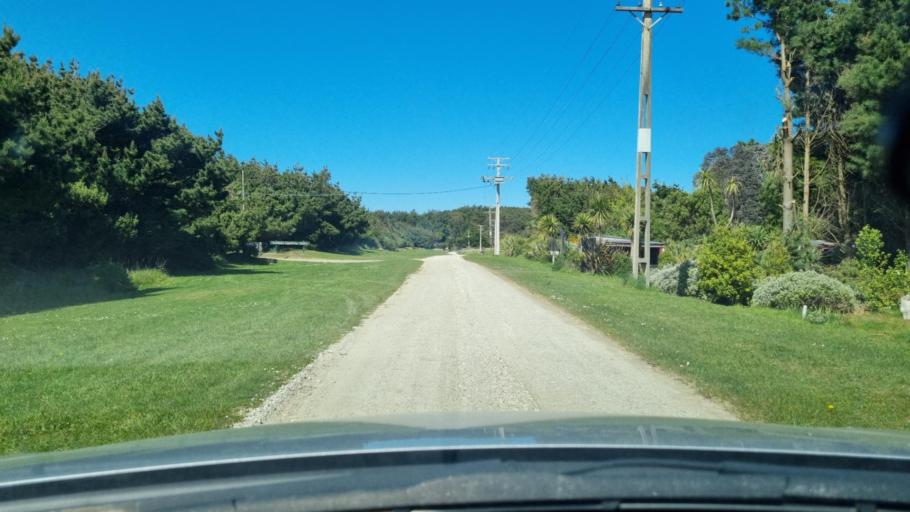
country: NZ
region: Southland
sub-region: Invercargill City
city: Invercargill
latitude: -46.4384
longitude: 168.2389
